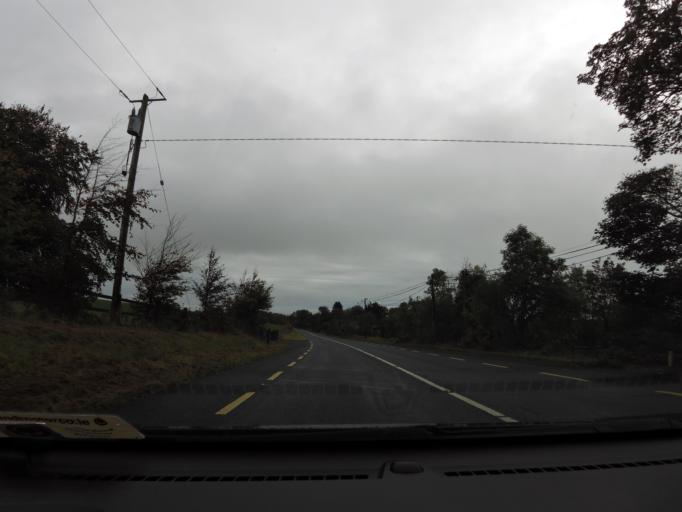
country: IE
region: Connaught
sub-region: County Galway
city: Tuam
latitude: 53.5688
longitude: -8.7888
